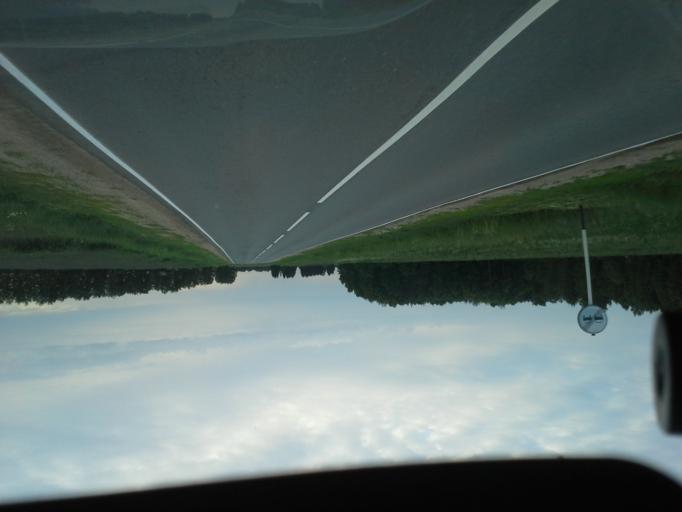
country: RU
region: Ivanovo
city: Gavrilov Posad
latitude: 56.5848
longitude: 40.2203
